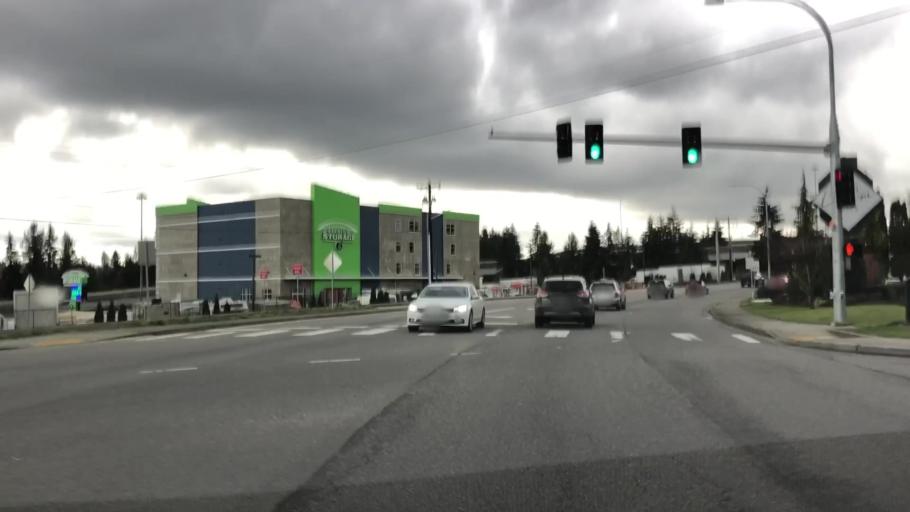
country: US
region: Washington
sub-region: Snohomish County
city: Everett
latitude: 47.9228
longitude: -122.2072
